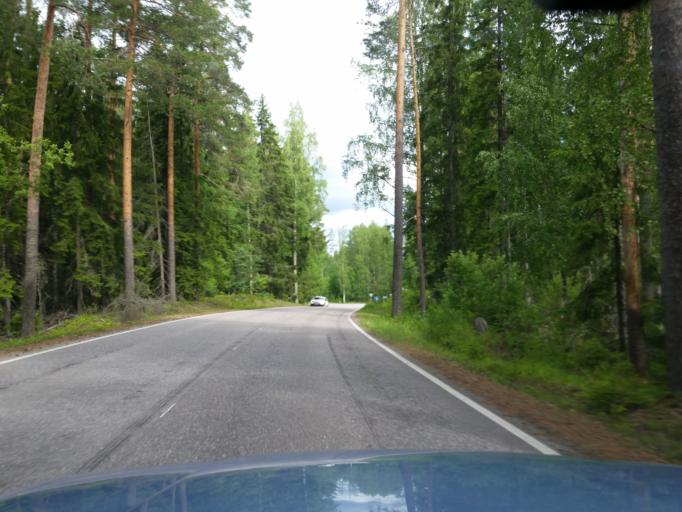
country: FI
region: Southern Savonia
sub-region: Savonlinna
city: Sulkava
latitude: 61.7984
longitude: 28.4123
